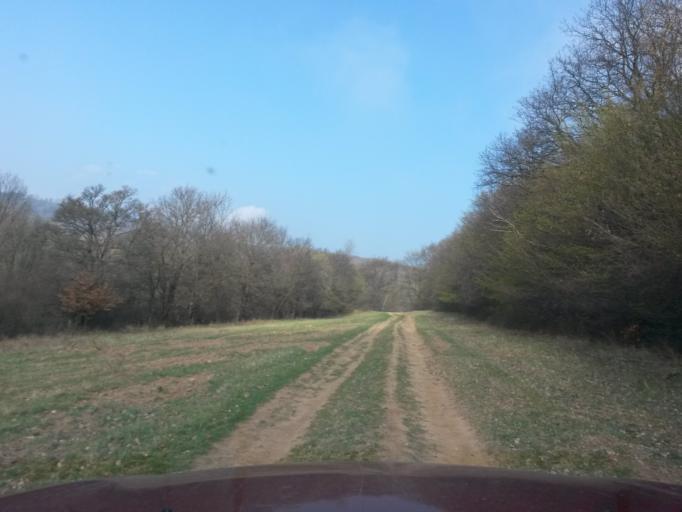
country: SK
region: Presovsky
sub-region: Okres Presov
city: Presov
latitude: 48.9225
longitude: 21.1666
